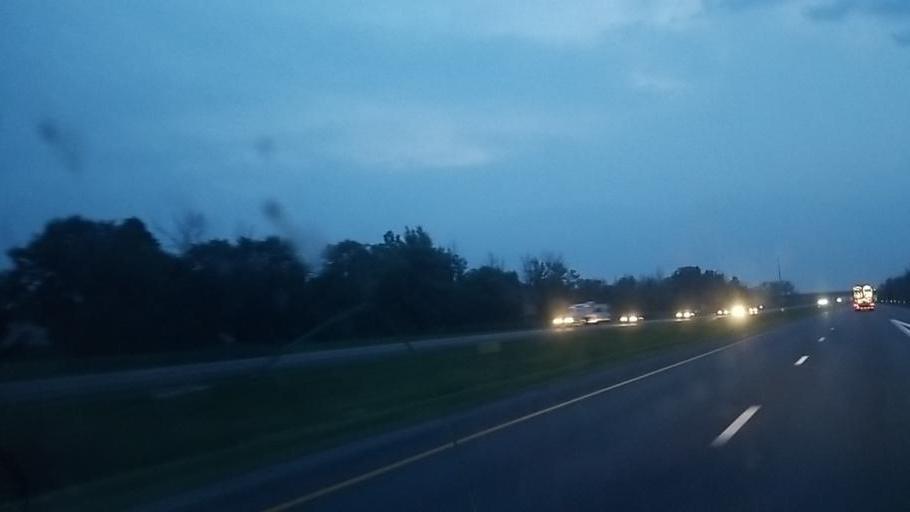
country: US
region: New York
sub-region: Onondaga County
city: East Syracuse
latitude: 43.0949
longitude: -76.0464
